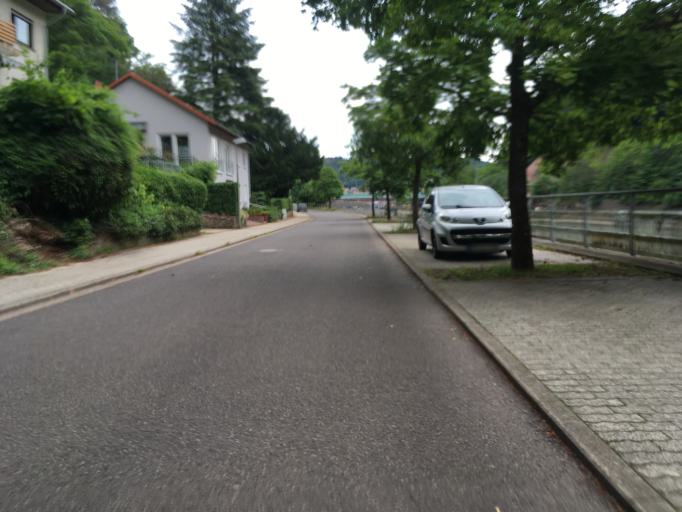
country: DE
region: Saarland
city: Mettlach
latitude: 49.4917
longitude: 6.5847
